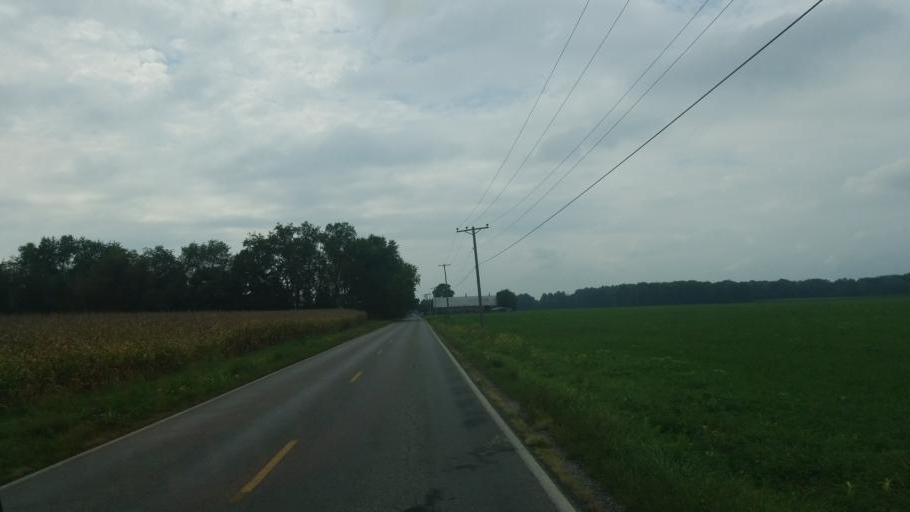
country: US
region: Ohio
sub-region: Wayne County
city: Creston
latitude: 40.9606
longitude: -81.8673
